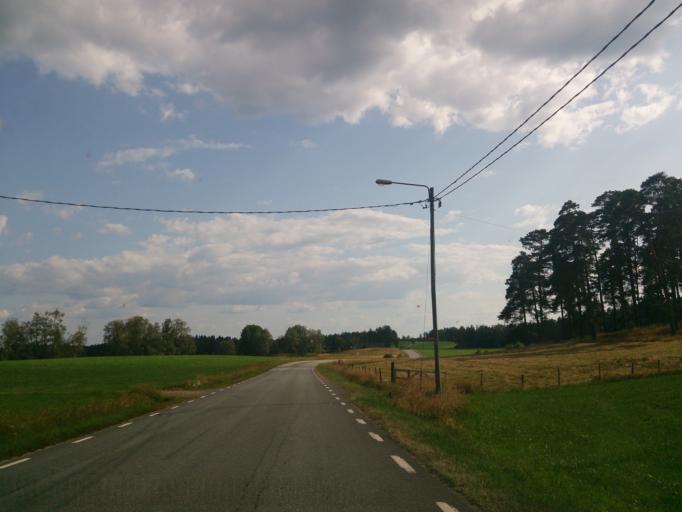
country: SE
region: Joenkoeping
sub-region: Gislaveds Kommun
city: Reftele
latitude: 57.1488
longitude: 13.6327
